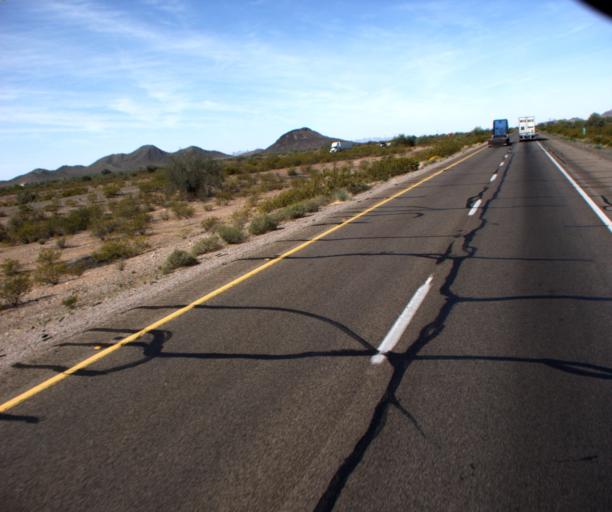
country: US
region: Arizona
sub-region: Maricopa County
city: Buckeye
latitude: 33.5073
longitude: -112.9894
